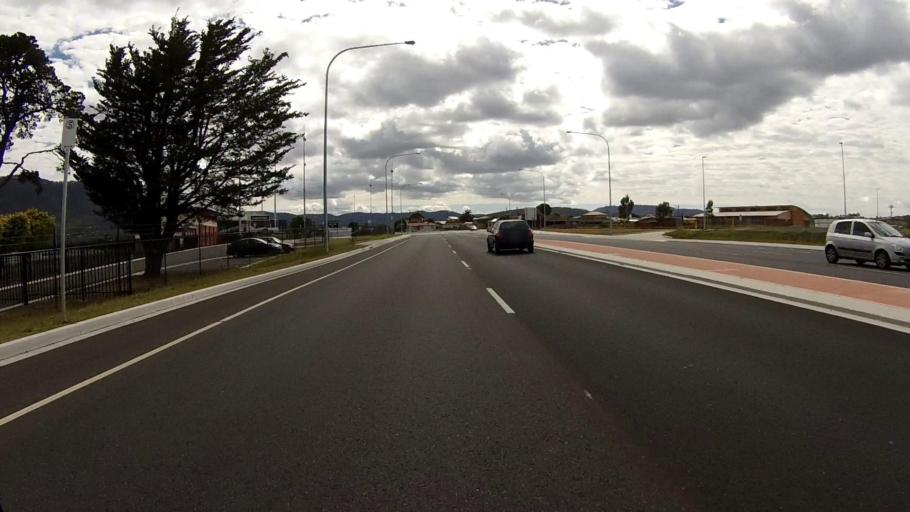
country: AU
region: Tasmania
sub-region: Glenorchy
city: Goodwood
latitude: -42.8271
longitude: 147.2864
